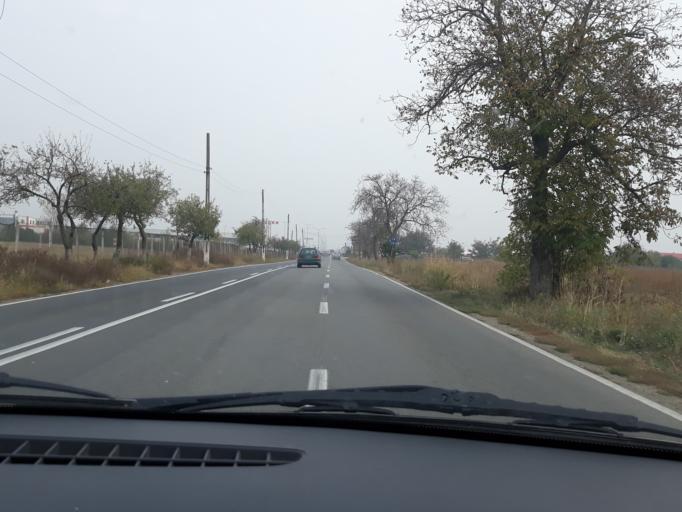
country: RO
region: Bihor
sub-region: Comuna Santandrei
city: Santandrei
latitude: 47.0507
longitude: 21.8821
